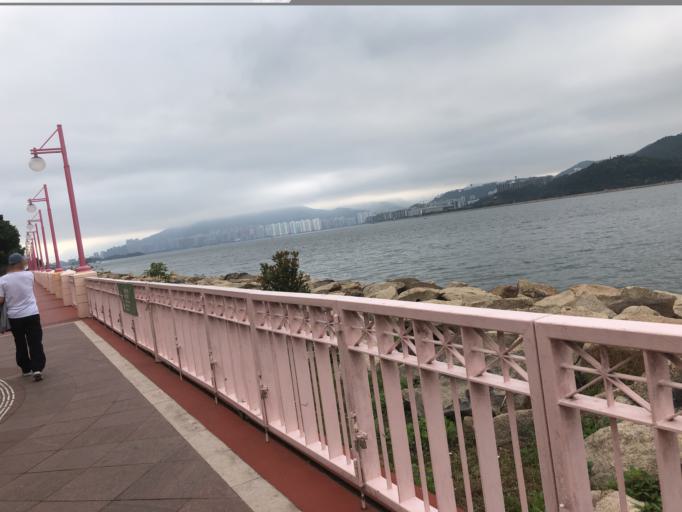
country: HK
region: Tai Po
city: Tai Po
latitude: 22.4525
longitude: 114.1871
